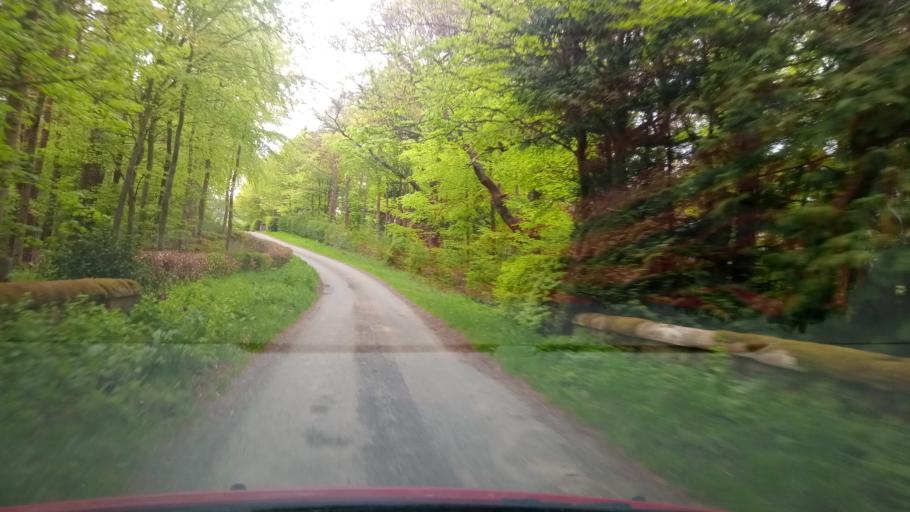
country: GB
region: Scotland
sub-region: The Scottish Borders
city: Saint Boswells
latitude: 55.5132
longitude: -2.6665
